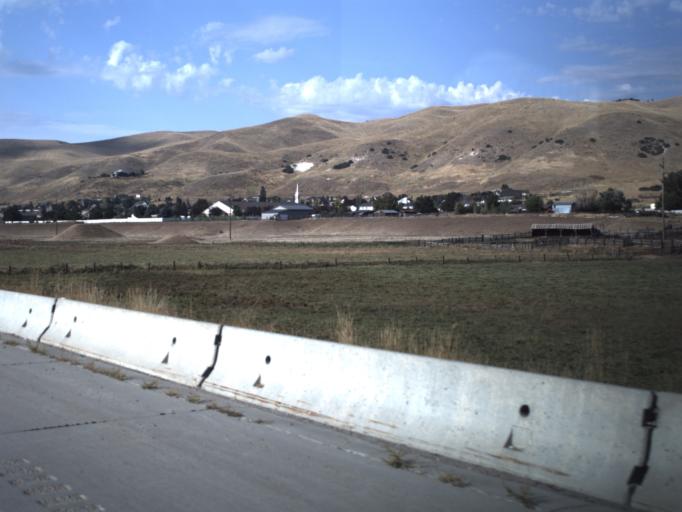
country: US
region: Utah
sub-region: Morgan County
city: Mountain Green
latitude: 41.0994
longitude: -111.7424
